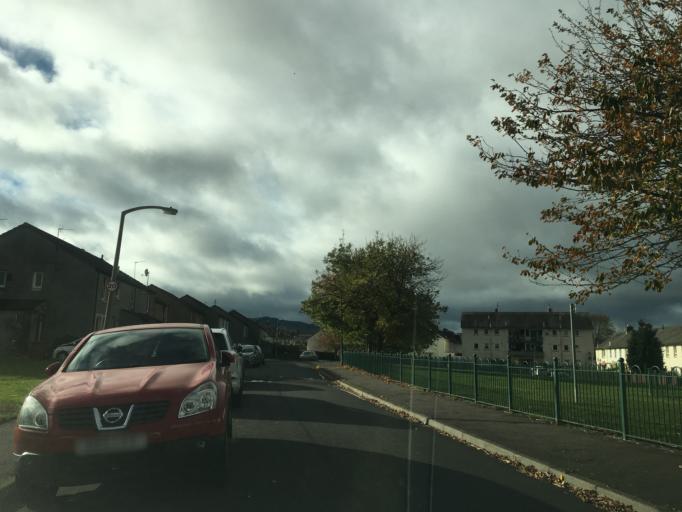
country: GB
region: Scotland
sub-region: Midlothian
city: Loanhead
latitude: 55.9206
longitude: -3.1511
